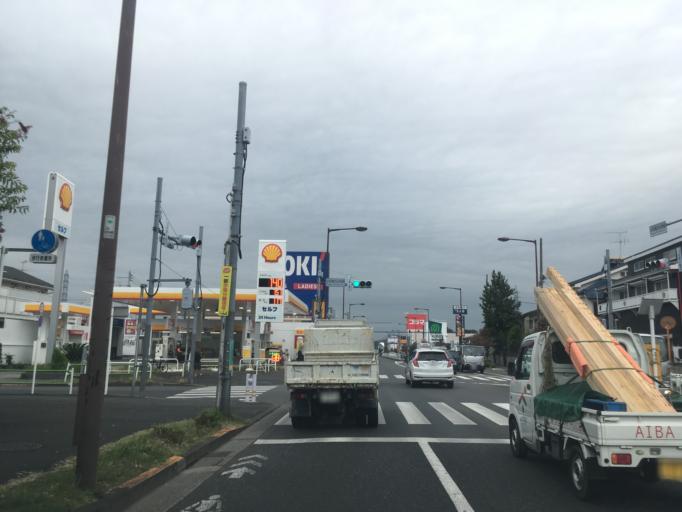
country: JP
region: Tokyo
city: Higashimurayama-shi
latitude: 35.7345
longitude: 139.4656
